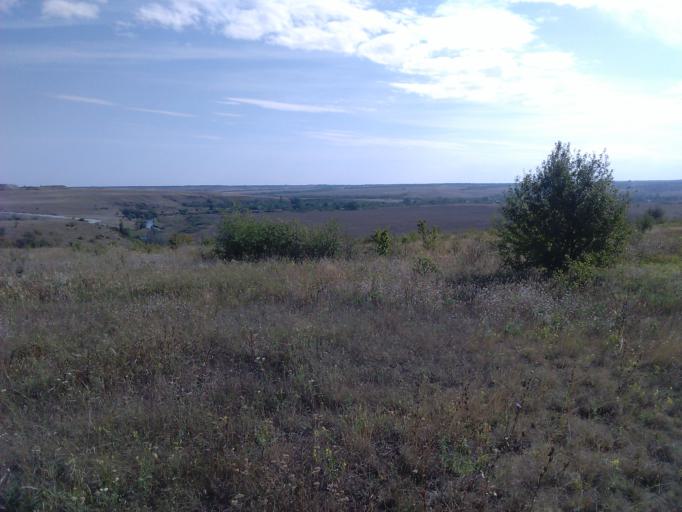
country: RU
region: Rostov
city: Gornyy
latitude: 47.8888
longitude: 40.2410
